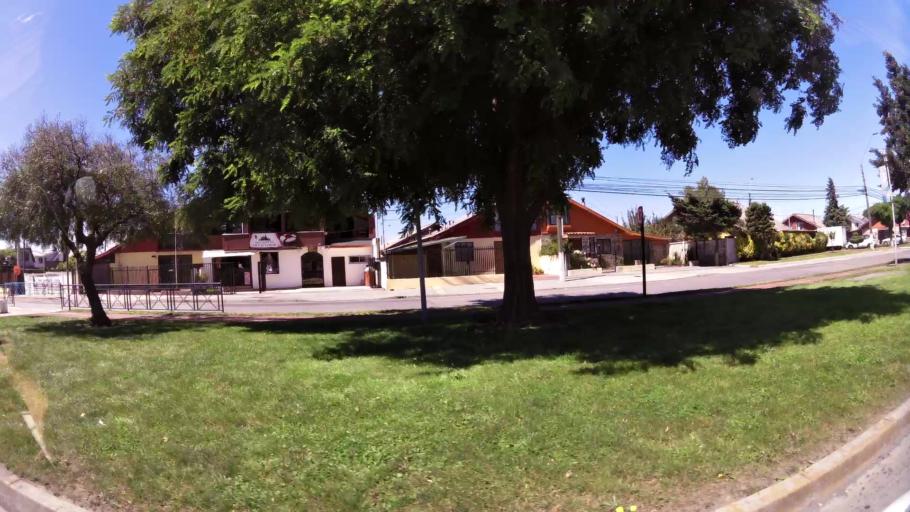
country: CL
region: Biobio
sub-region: Provincia de Concepcion
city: Talcahuano
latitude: -36.7536
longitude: -73.0921
